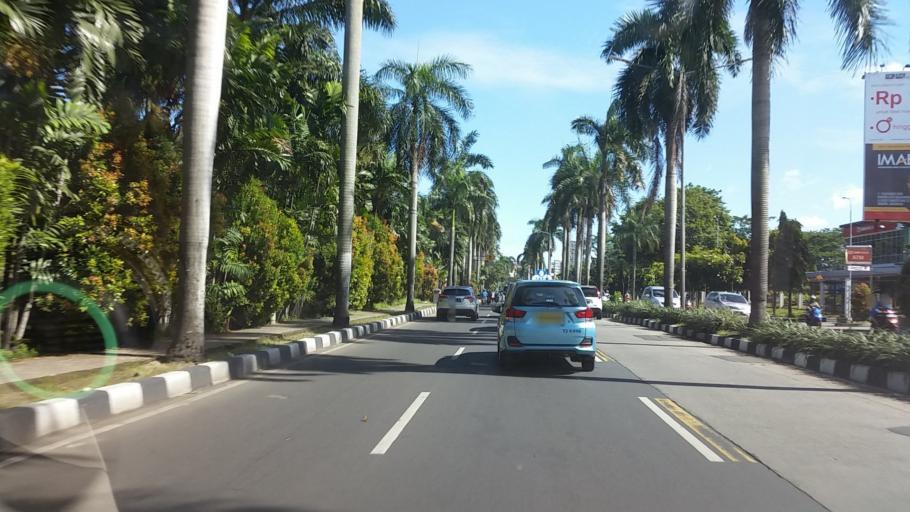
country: ID
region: Banten
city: South Tangerang
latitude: -6.2732
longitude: 106.7827
